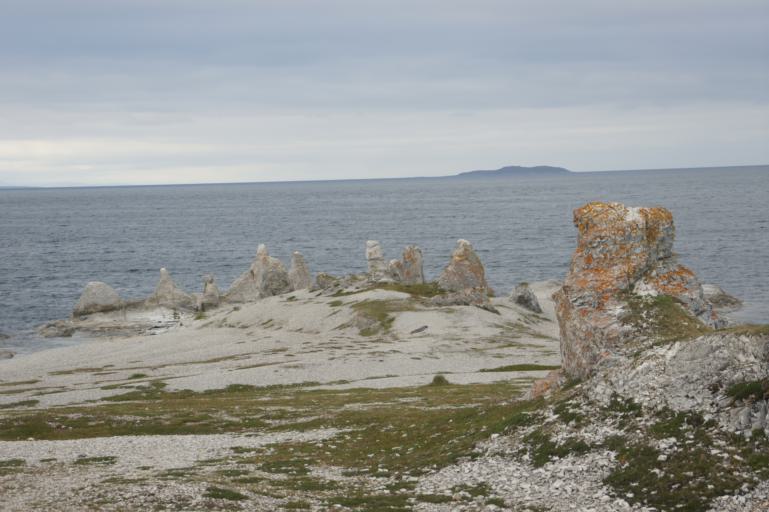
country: NO
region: Finnmark Fylke
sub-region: Porsanger
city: Lakselv
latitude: 70.3048
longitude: 25.1767
